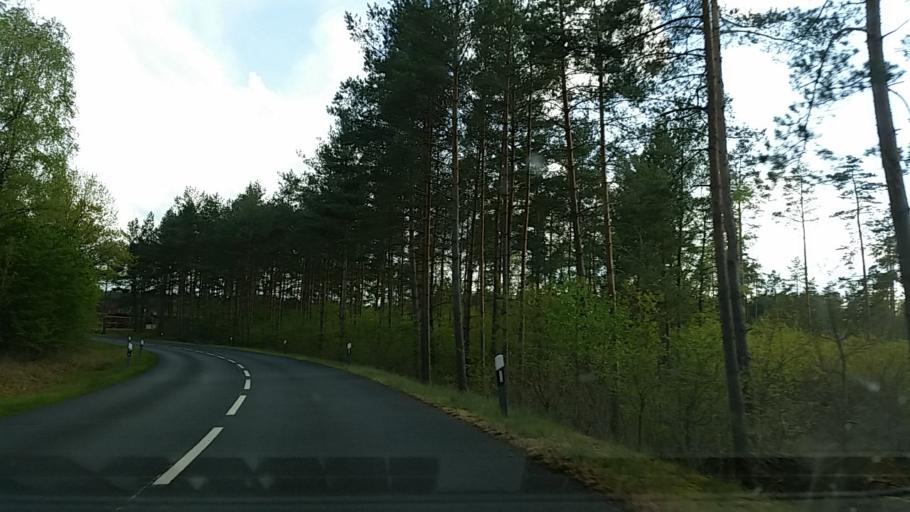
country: DE
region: Lower Saxony
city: Bodenteich
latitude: 52.8489
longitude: 10.6604
